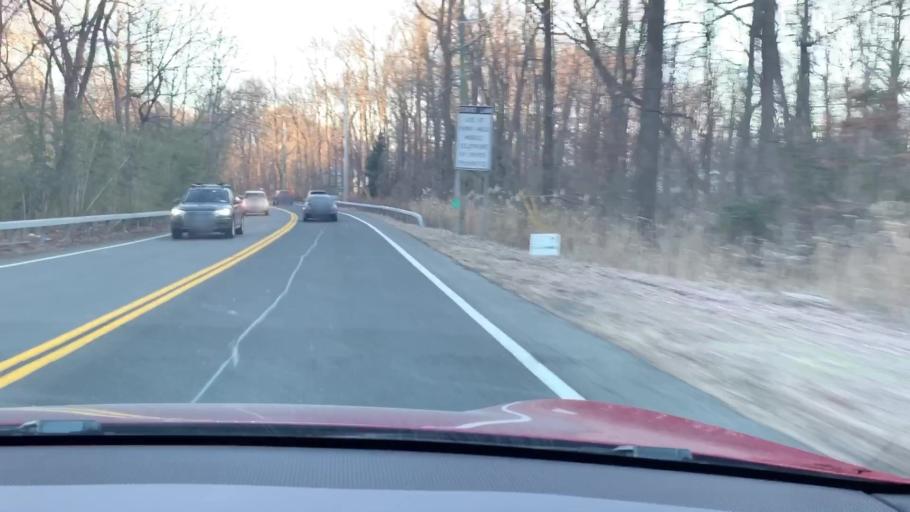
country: US
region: New York
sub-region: Rockland County
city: Sparkill
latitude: 41.0077
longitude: -73.9143
